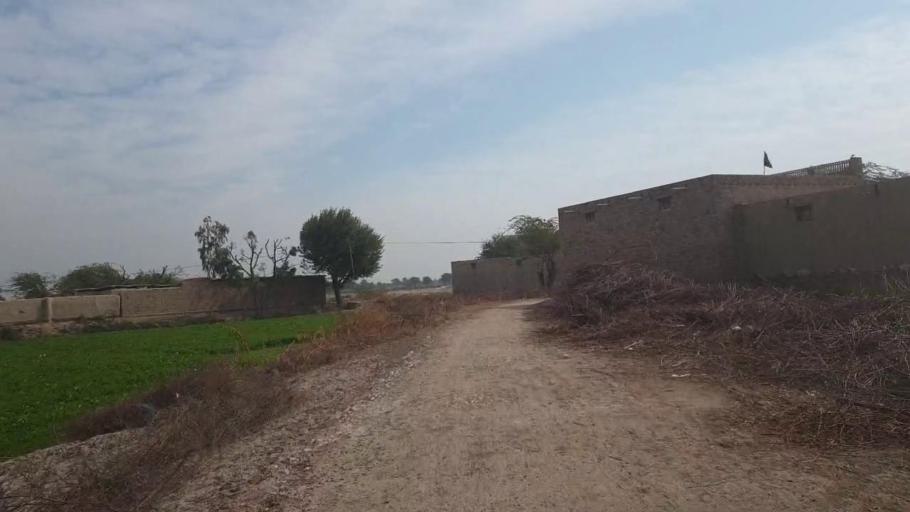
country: PK
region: Sindh
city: Nawabshah
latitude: 26.1072
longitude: 68.4829
